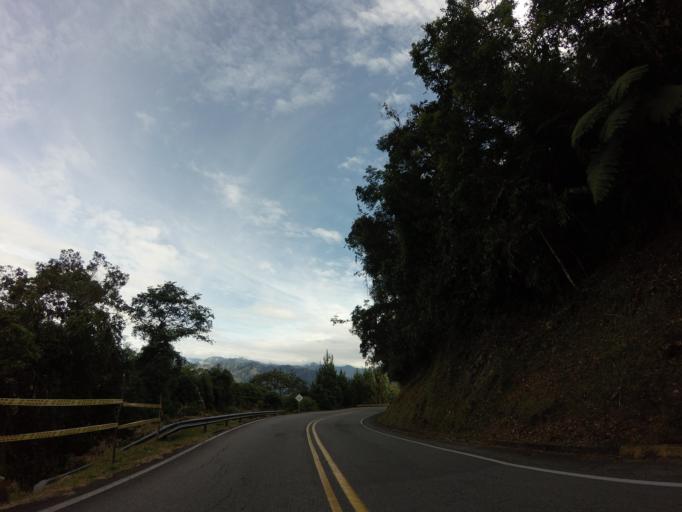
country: CO
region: Tolima
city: Herveo
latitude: 5.1452
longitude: -75.1546
